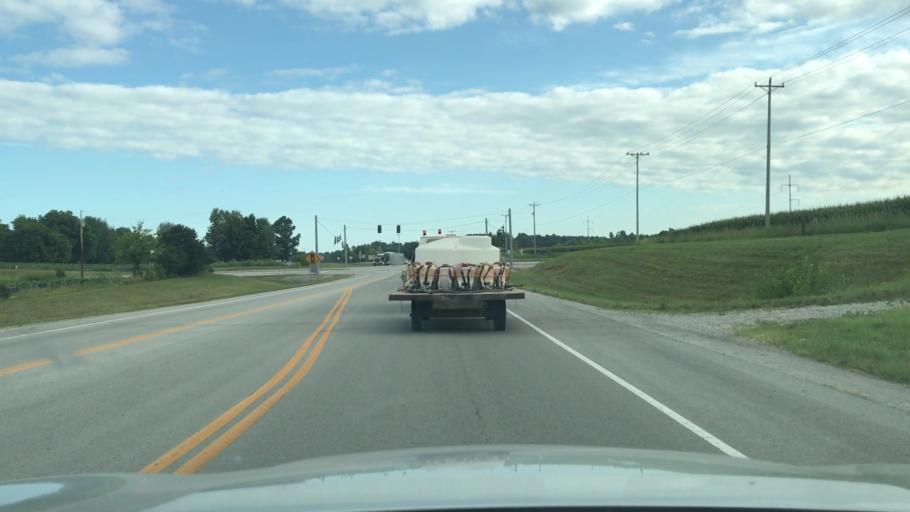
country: US
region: Kentucky
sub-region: Todd County
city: Elkton
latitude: 36.8227
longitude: -87.1510
